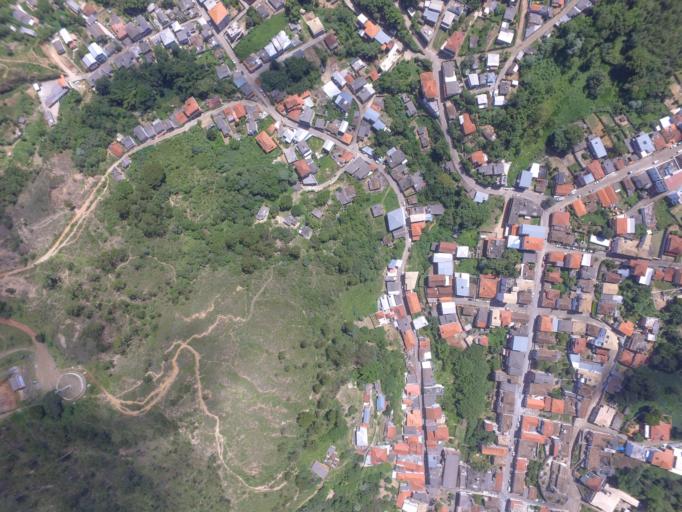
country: BR
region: Minas Gerais
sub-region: Tiradentes
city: Tiradentes
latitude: -21.0553
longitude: -44.0770
